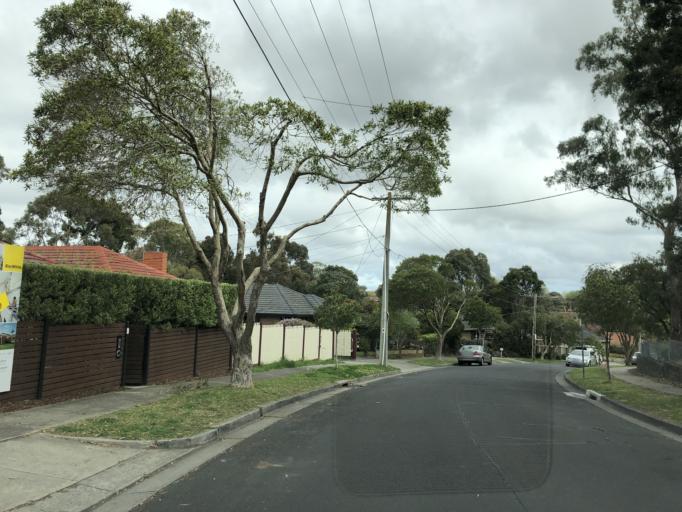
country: AU
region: Victoria
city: Burwood East
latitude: -37.8485
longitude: 145.1483
